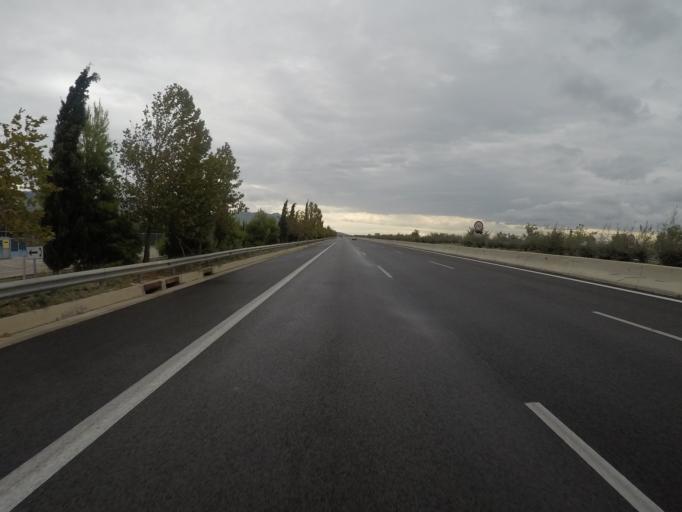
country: GR
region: Attica
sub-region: Nomarchia Dytikis Attikis
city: Nea Peramos
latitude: 38.0086
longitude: 23.4005
